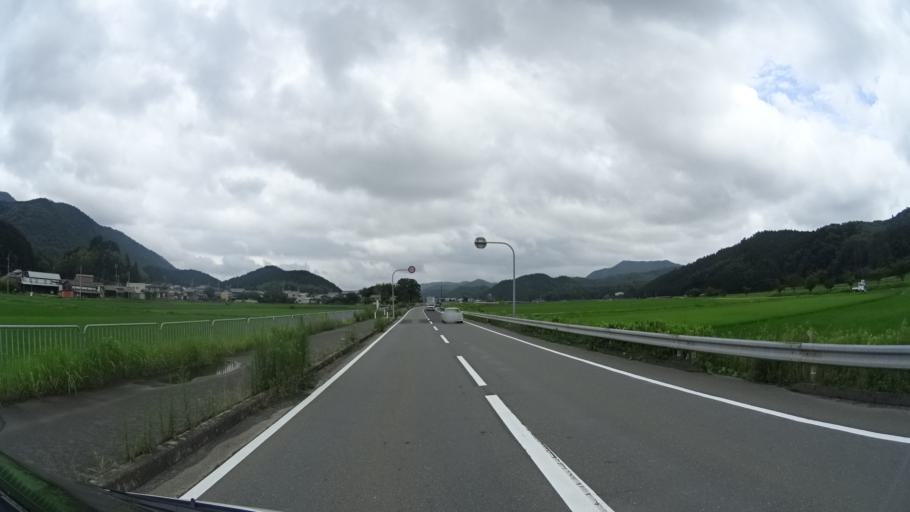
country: JP
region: Kyoto
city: Kameoka
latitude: 35.0370
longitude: 135.4852
